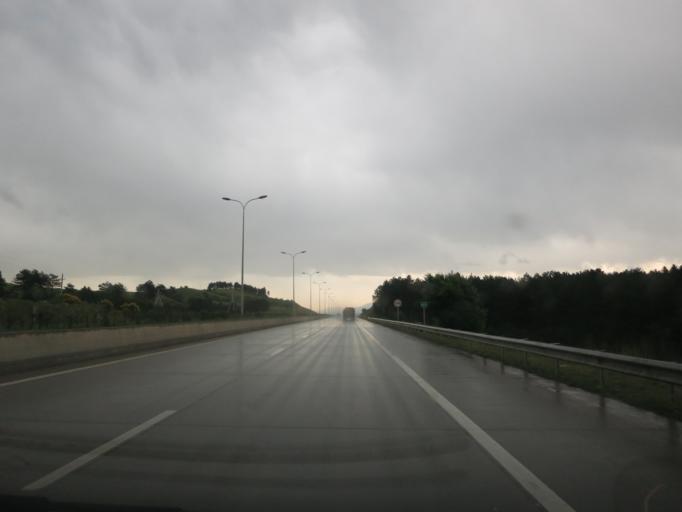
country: GE
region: Shida Kartli
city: Gori
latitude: 42.0146
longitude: 44.0320
